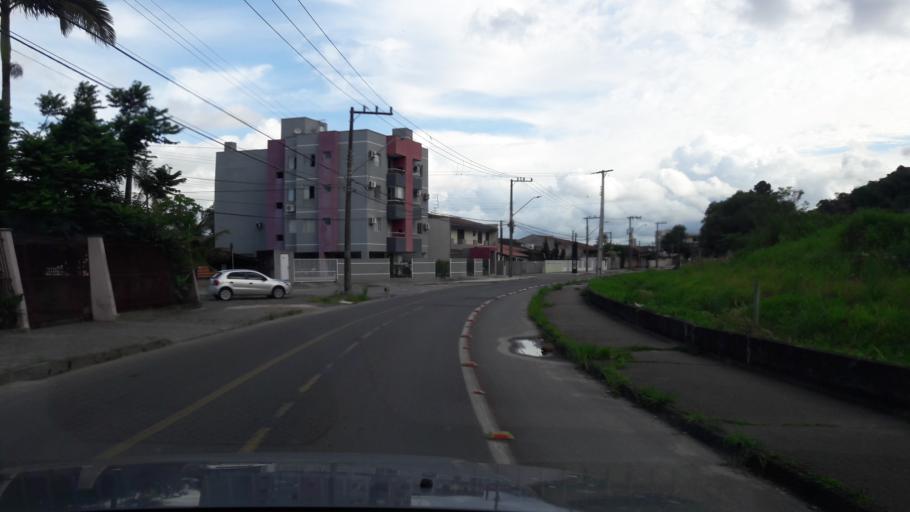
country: BR
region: Santa Catarina
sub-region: Joinville
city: Joinville
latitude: -26.3231
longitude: -48.8221
